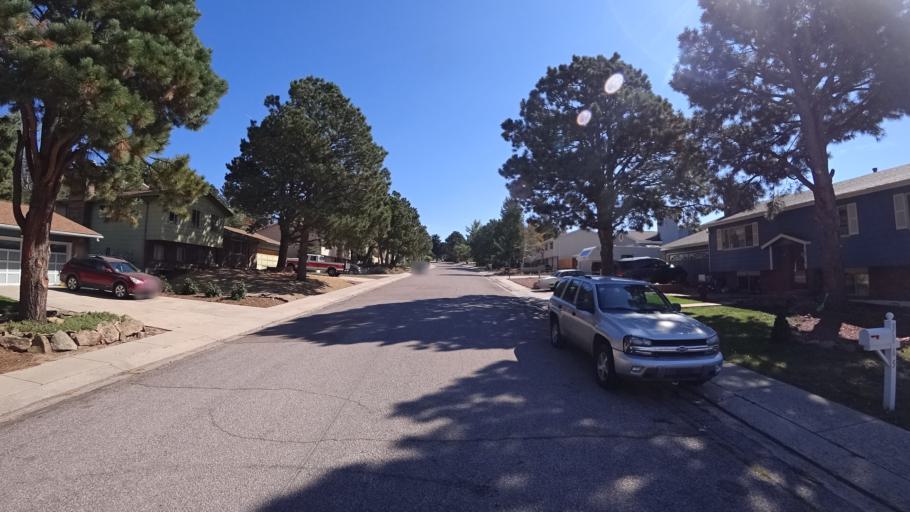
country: US
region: Colorado
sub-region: El Paso County
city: Cimarron Hills
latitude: 38.9117
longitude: -104.7687
